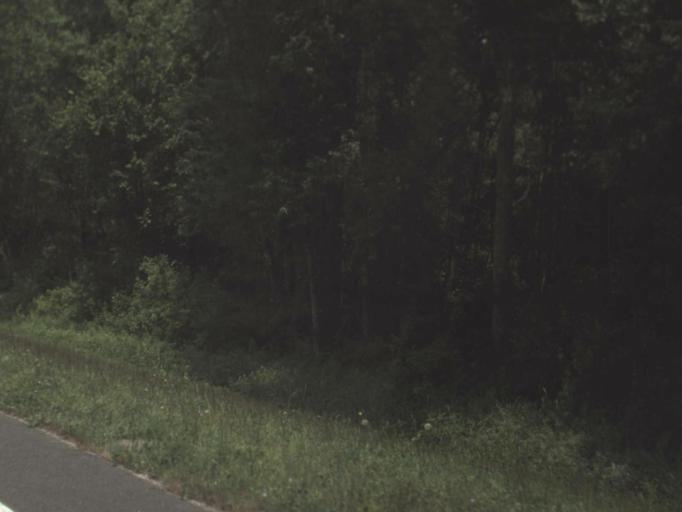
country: US
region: Florida
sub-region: Columbia County
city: Five Points
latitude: 30.2767
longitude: -82.6313
